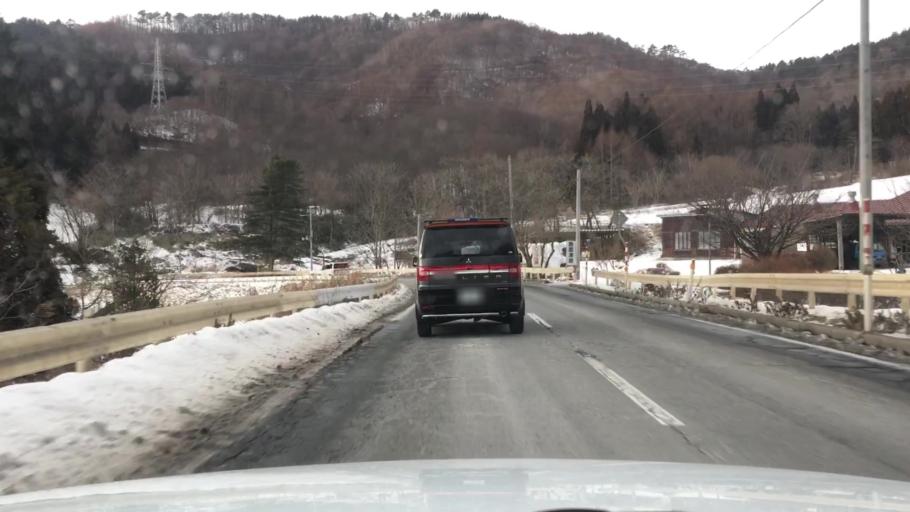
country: JP
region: Iwate
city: Morioka-shi
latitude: 39.6719
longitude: 141.3298
